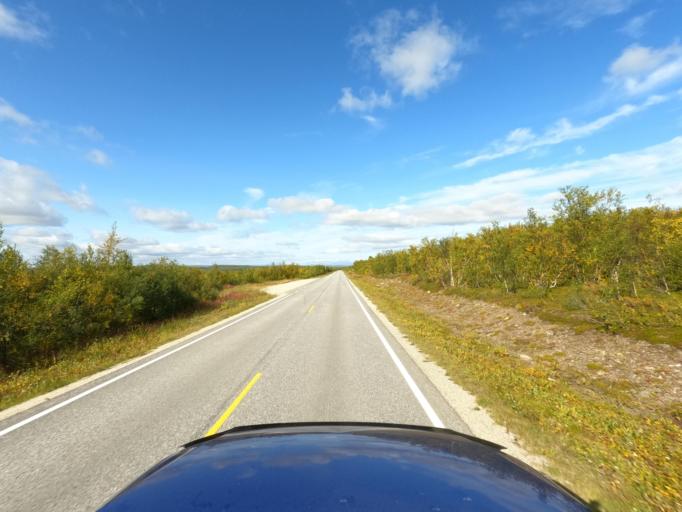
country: NO
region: Finnmark Fylke
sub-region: Karasjok
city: Karasjohka
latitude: 69.5609
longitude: 25.3900
